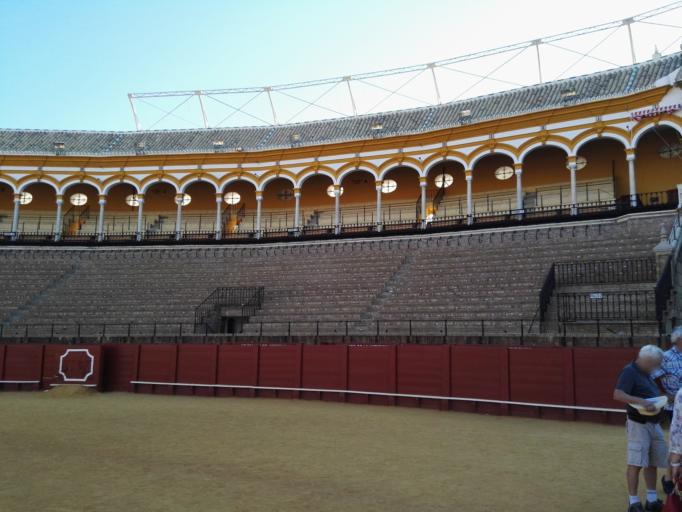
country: ES
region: Andalusia
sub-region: Provincia de Sevilla
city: Sevilla
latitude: 37.3859
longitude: -5.9986
